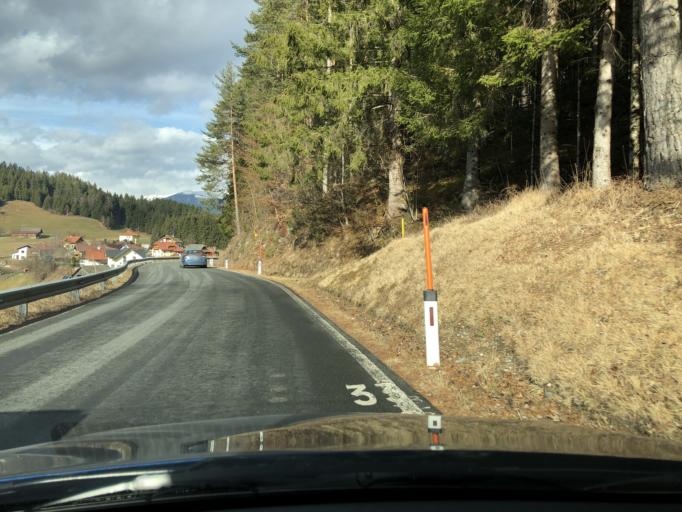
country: AT
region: Carinthia
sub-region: Politischer Bezirk Villach Land
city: Paternion
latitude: 46.7116
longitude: 13.6106
